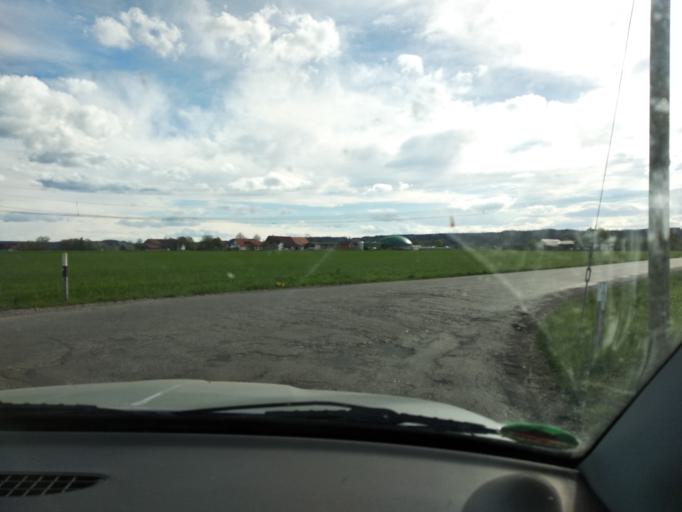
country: DE
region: Bavaria
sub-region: Swabia
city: Lachen
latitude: 47.9275
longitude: 10.2267
